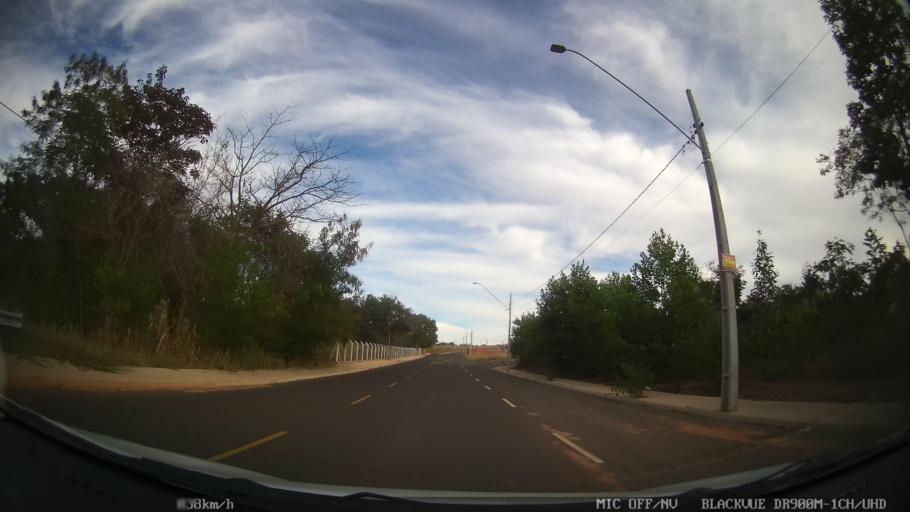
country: BR
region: Sao Paulo
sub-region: Catanduva
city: Catanduva
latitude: -21.1410
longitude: -49.0051
